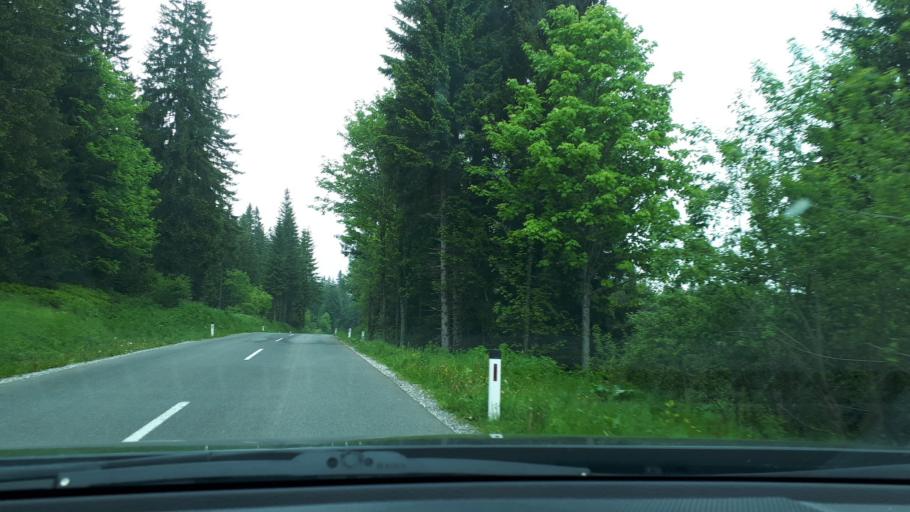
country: AT
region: Styria
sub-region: Politischer Bezirk Voitsberg
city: Modriach
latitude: 46.9130
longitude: 15.0304
